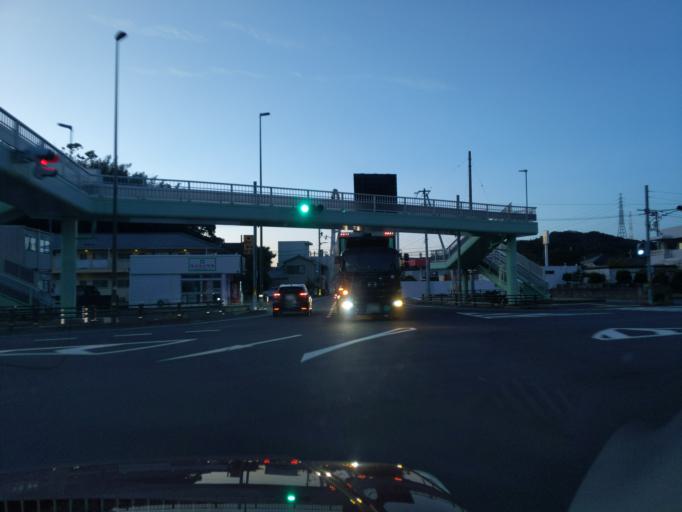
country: JP
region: Tokushima
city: Anan
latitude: 33.8879
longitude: 134.6527
